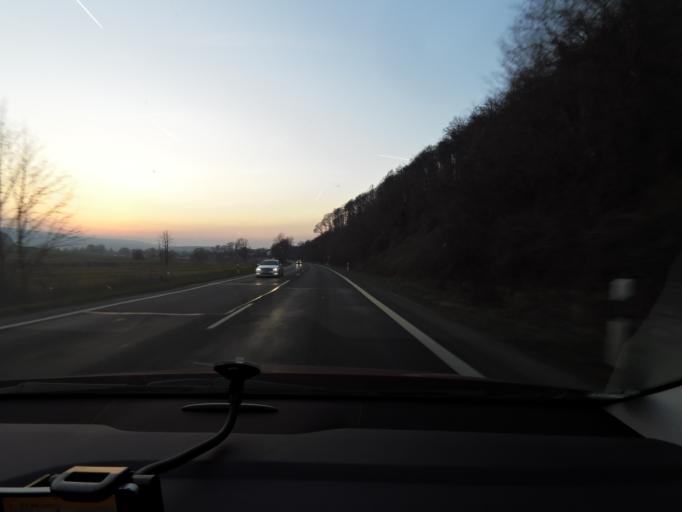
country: DE
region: Lower Saxony
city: Juhnde
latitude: 51.3893
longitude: 9.7941
